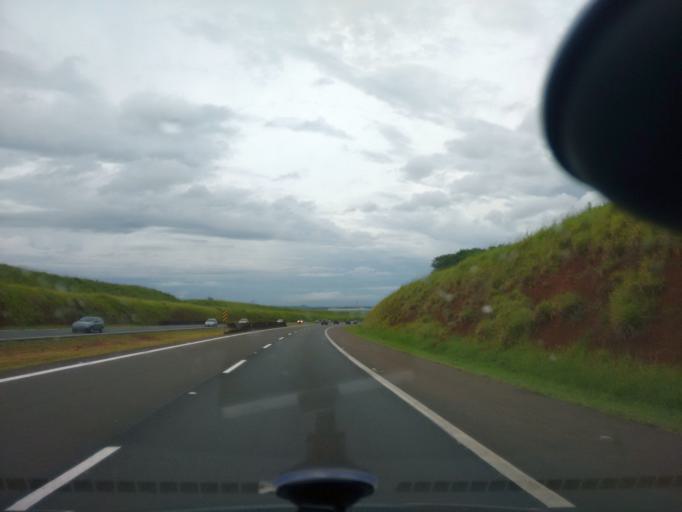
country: BR
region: Sao Paulo
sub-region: Cordeiropolis
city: Cordeiropolis
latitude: -22.5325
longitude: -47.4472
